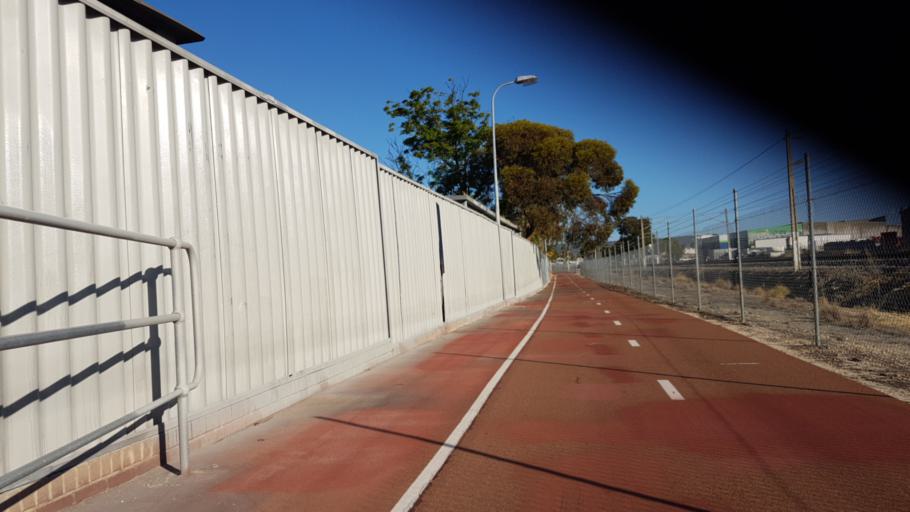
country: AU
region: Western Australia
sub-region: Gosnells
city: Maddington
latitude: -32.0472
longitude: 115.9793
